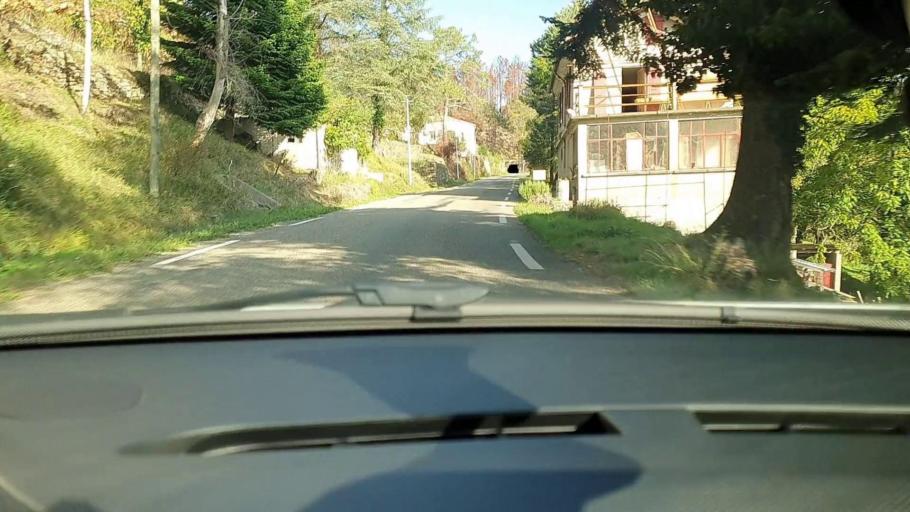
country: FR
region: Languedoc-Roussillon
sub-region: Departement du Gard
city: Besseges
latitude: 44.3078
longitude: 4.0919
